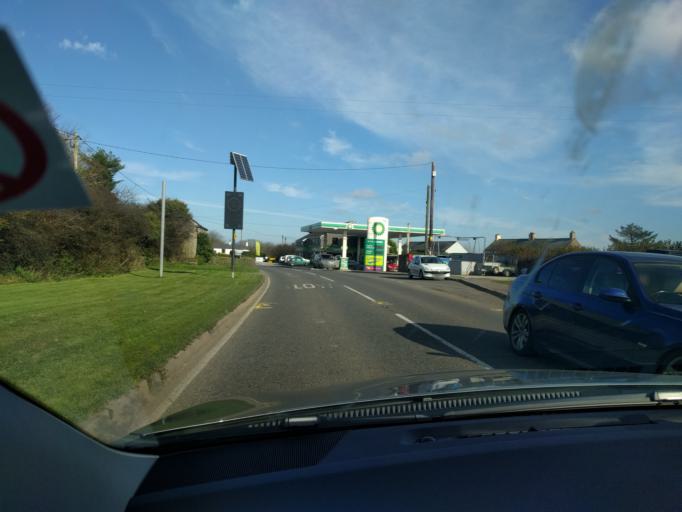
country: GB
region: England
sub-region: Cornwall
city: Camelford
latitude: 50.6115
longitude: -4.6875
